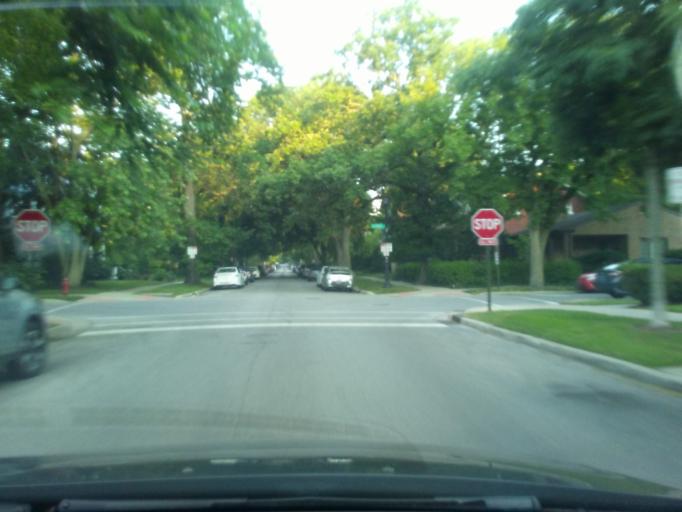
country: US
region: Illinois
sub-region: Cook County
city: Evanston
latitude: 42.0317
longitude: -87.6820
